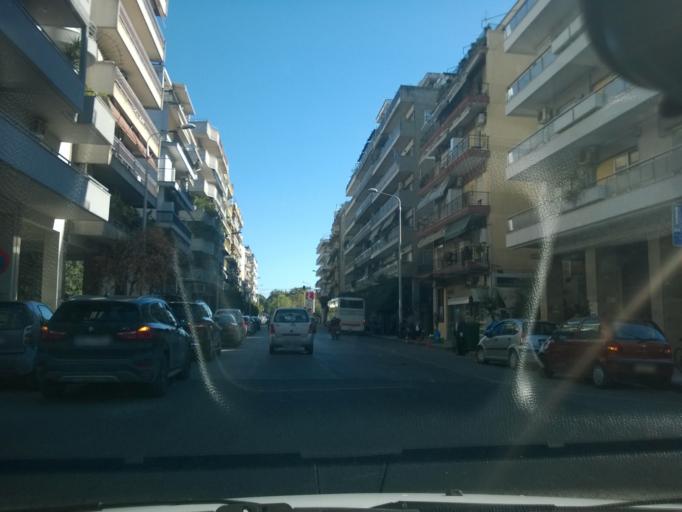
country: GR
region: Central Macedonia
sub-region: Nomos Thessalonikis
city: Kalamaria
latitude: 40.5986
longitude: 22.9520
